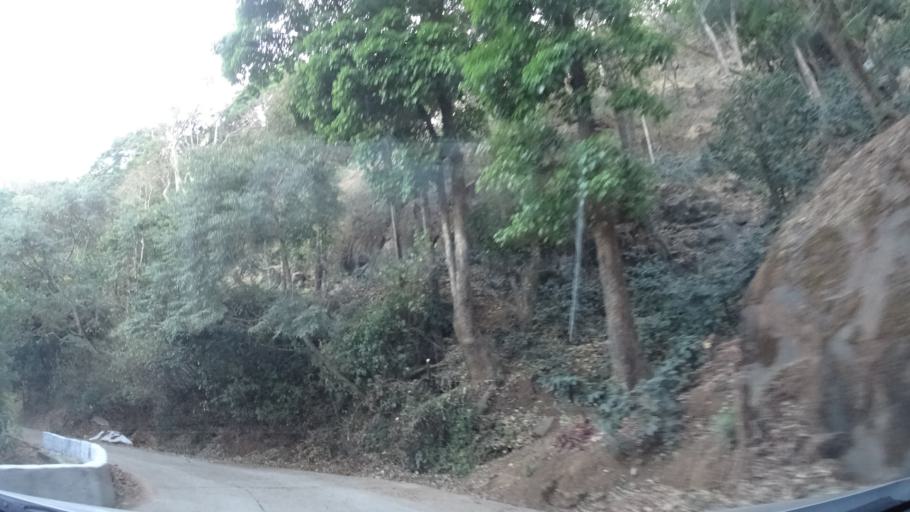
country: IN
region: Karnataka
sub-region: Chikmagalur
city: Tarikere
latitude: 13.5579
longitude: 75.7505
